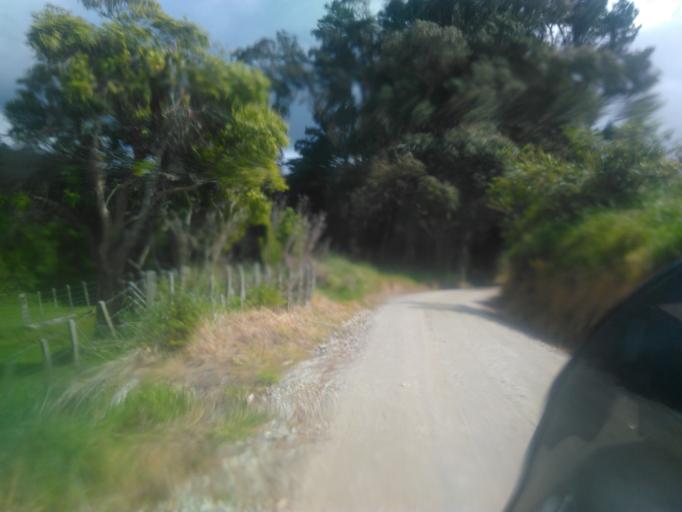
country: NZ
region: Hawke's Bay
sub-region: Wairoa District
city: Wairoa
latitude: -38.7612
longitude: 177.5951
